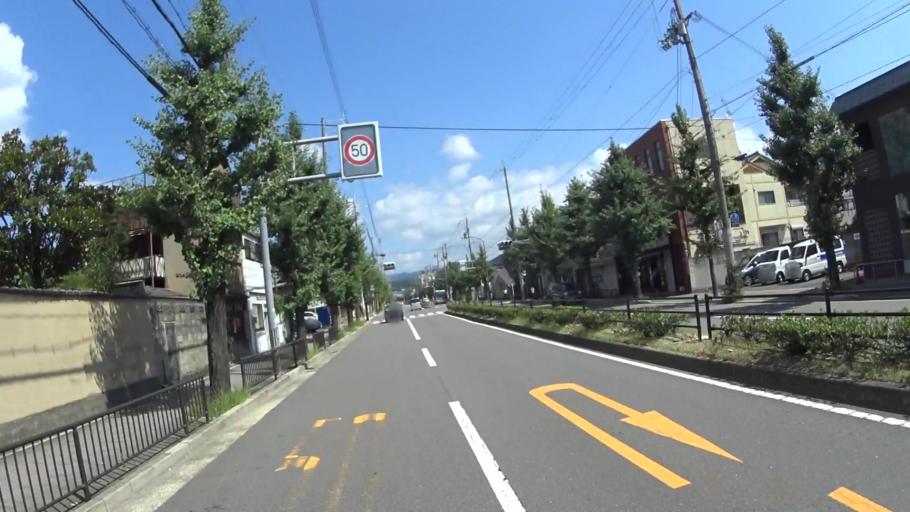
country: JP
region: Kyoto
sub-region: Kyoto-shi
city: Kamigyo-ku
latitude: 35.0399
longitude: 135.7708
